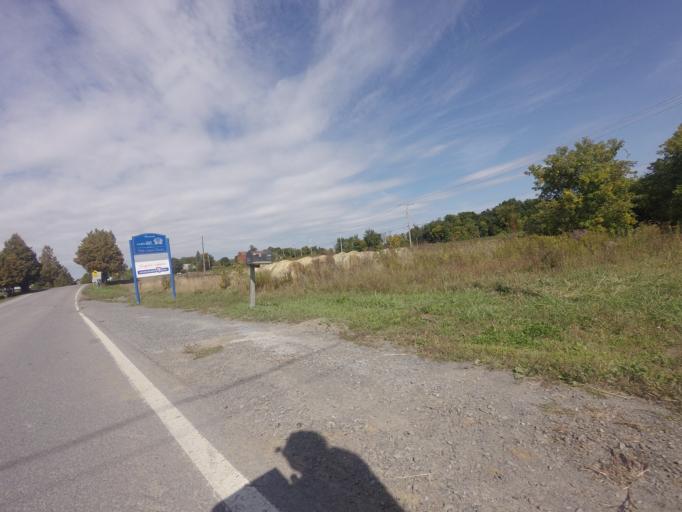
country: CA
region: Quebec
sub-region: Laurentides
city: Saint-Eustache
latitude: 45.6077
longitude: -73.9155
